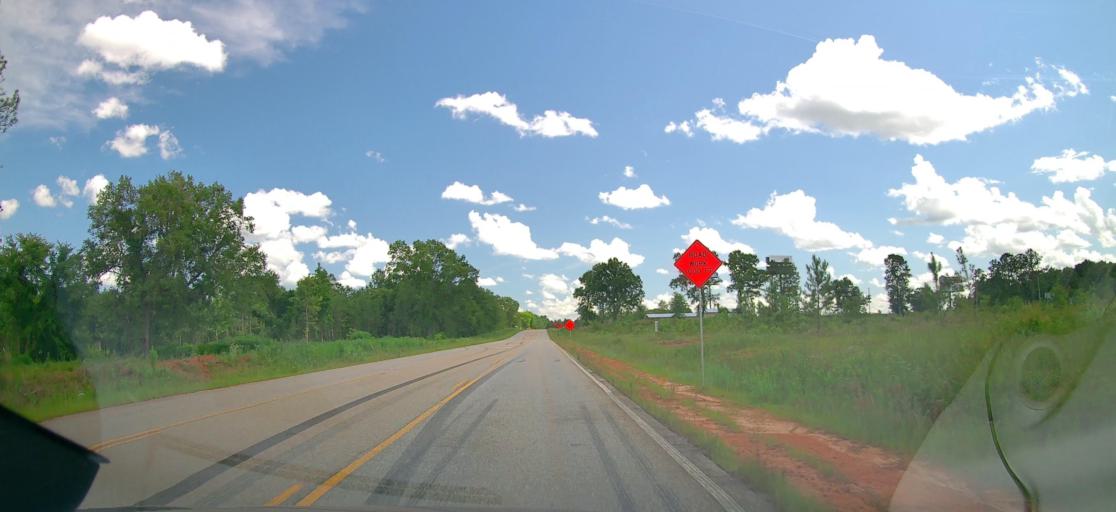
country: US
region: Georgia
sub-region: Peach County
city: Byron
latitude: 32.6062
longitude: -83.7406
